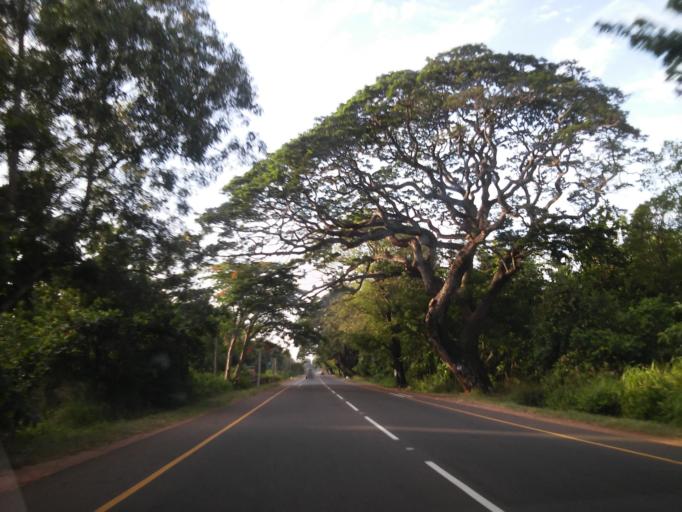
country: LK
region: North Central
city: Anuradhapura
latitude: 8.1446
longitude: 80.5463
